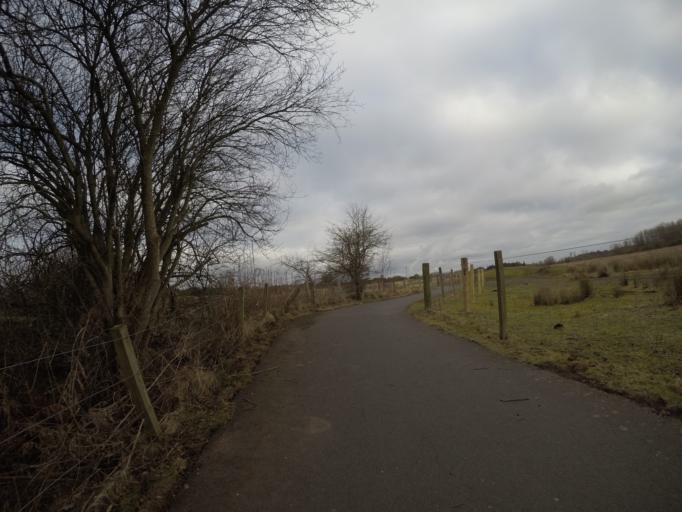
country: GB
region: Scotland
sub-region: North Ayrshire
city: Dreghorn
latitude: 55.5734
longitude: -4.6366
